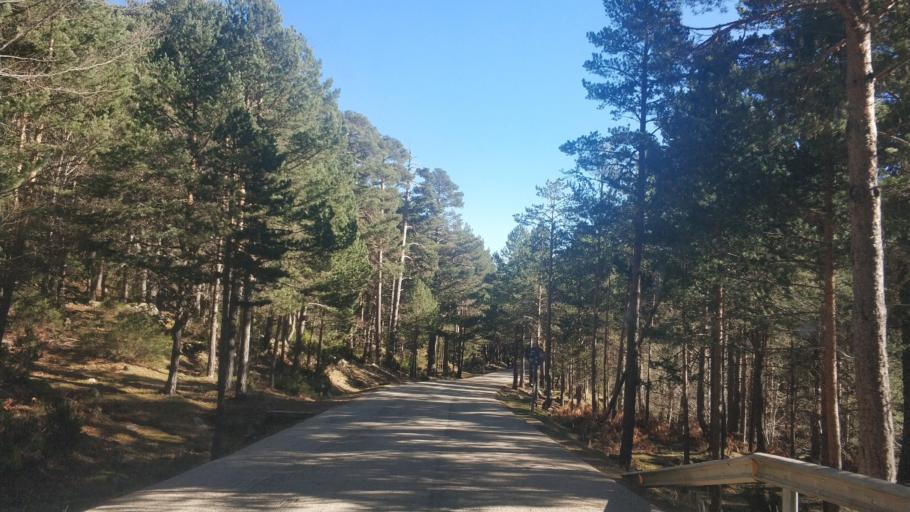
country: ES
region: Castille and Leon
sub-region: Provincia de Soria
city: Covaleda
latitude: 41.9978
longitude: -2.8369
